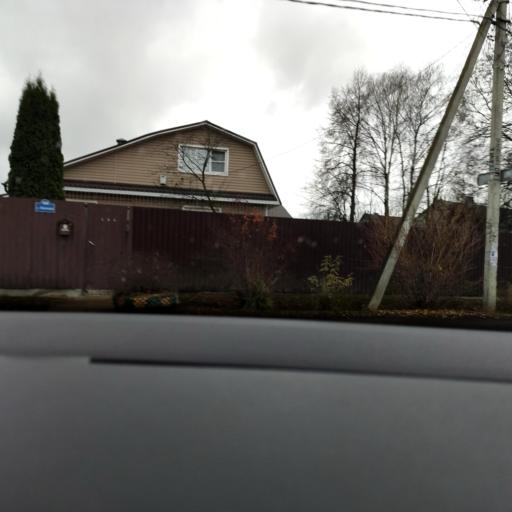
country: RU
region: Moscow
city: Gol'yanovo
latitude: 55.8326
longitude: 37.8356
